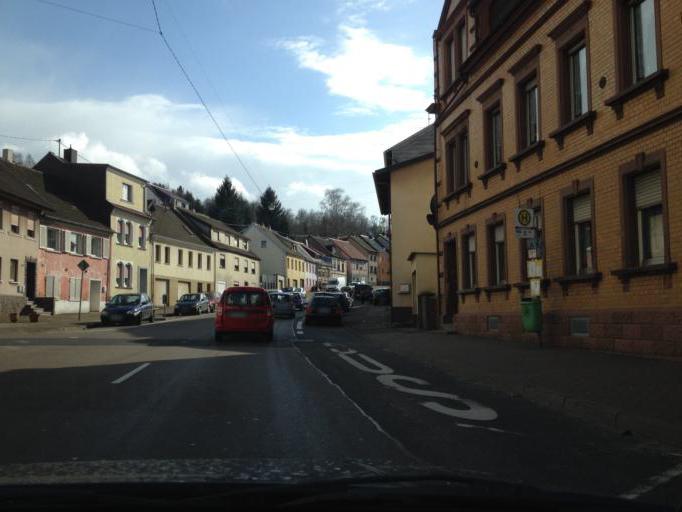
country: DE
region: Saarland
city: Neunkirchen
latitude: 49.3650
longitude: 7.1849
